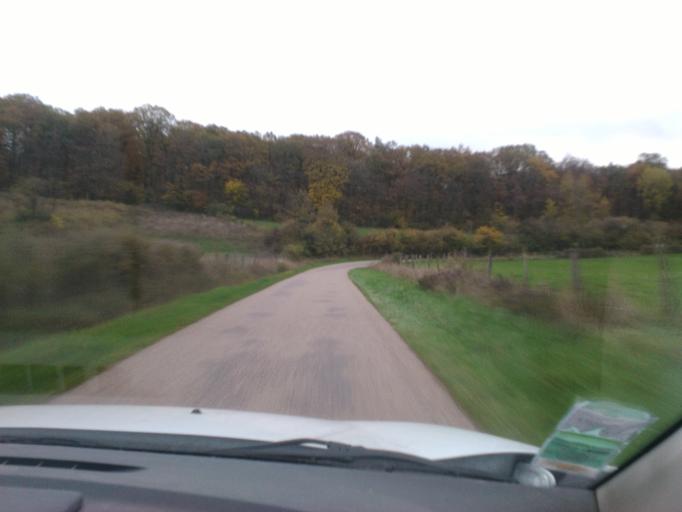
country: FR
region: Lorraine
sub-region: Departement des Vosges
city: Mirecourt
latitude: 48.3025
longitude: 6.2145
